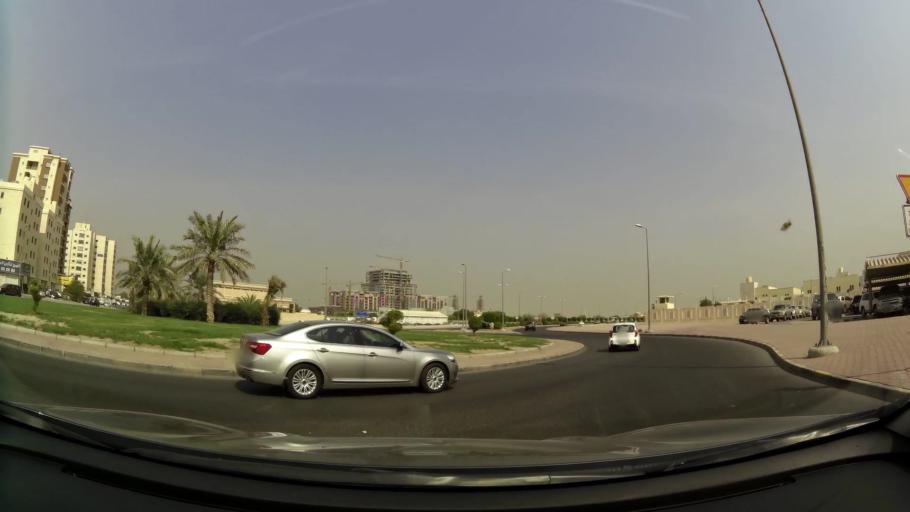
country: KW
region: Al Asimah
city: Ar Rabiyah
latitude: 29.3056
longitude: 47.9211
